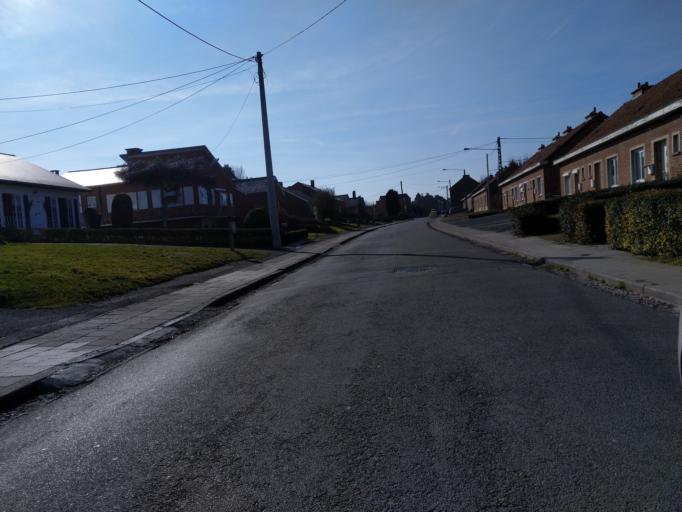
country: BE
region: Wallonia
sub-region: Province du Hainaut
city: Chasse Royale
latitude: 50.4307
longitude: 3.9308
